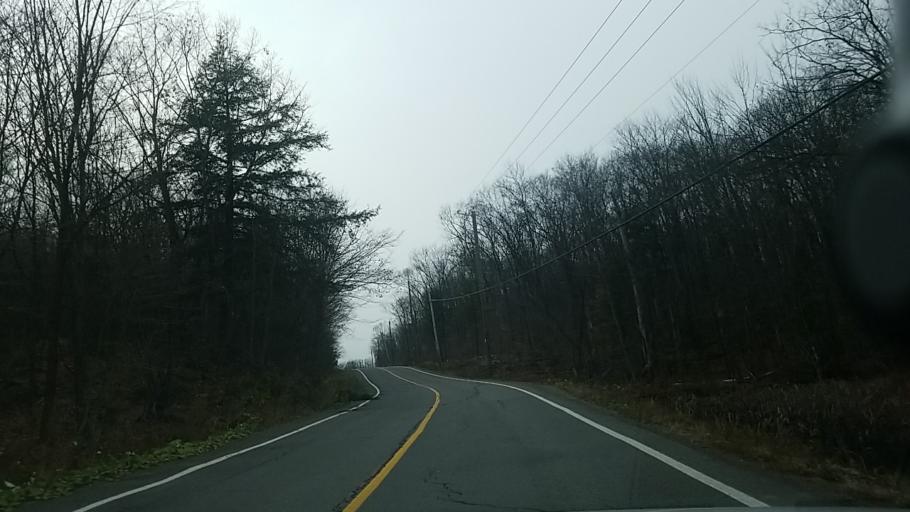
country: CA
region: Quebec
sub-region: Laurentides
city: Saint-Colomban
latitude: 45.7927
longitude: -74.1439
